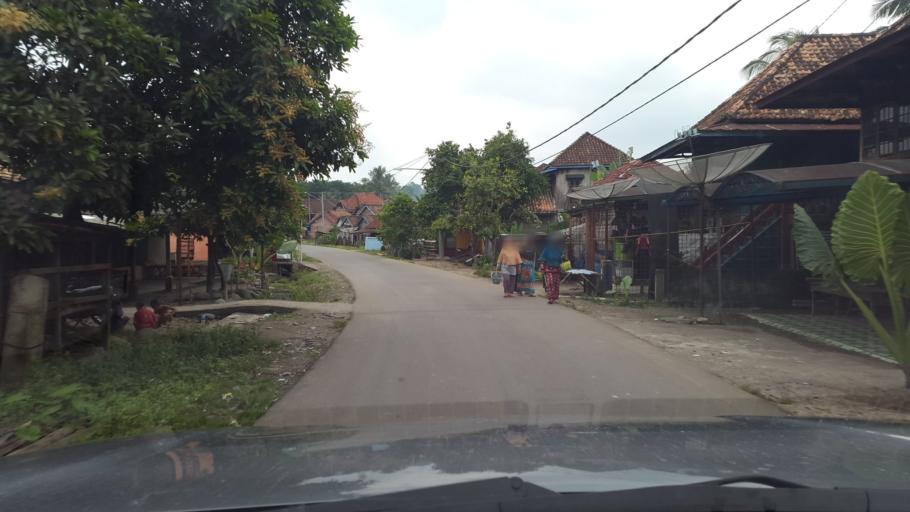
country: ID
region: South Sumatra
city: Gunungmenang
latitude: -3.1793
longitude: 104.0340
